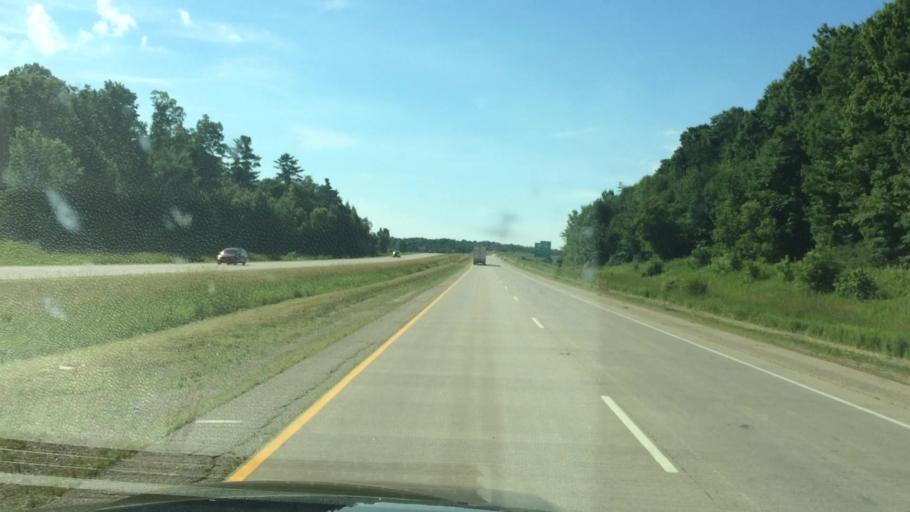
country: US
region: Wisconsin
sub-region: Shawano County
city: Bonduel
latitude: 44.7390
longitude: -88.4662
